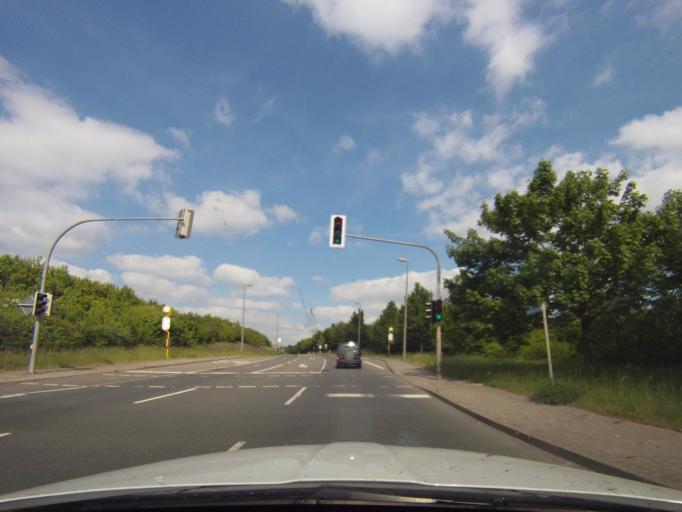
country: DE
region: Thuringia
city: Gera
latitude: 50.8601
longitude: 12.1020
